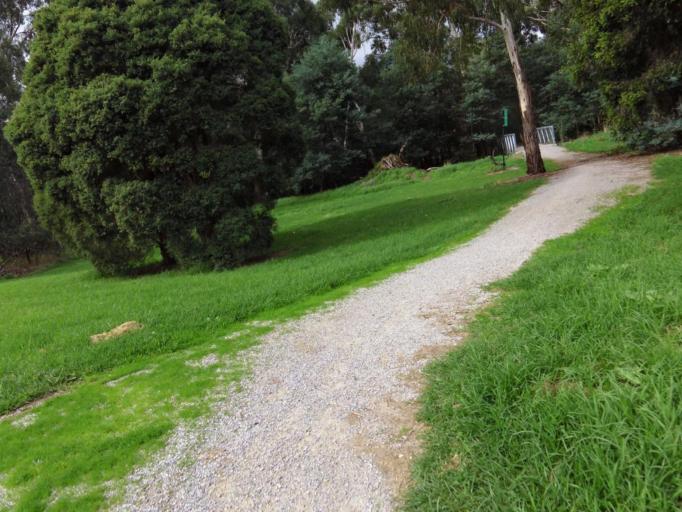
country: AU
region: Victoria
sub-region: Yarra Ranges
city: Mount Evelyn
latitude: -37.7782
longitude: 145.3608
